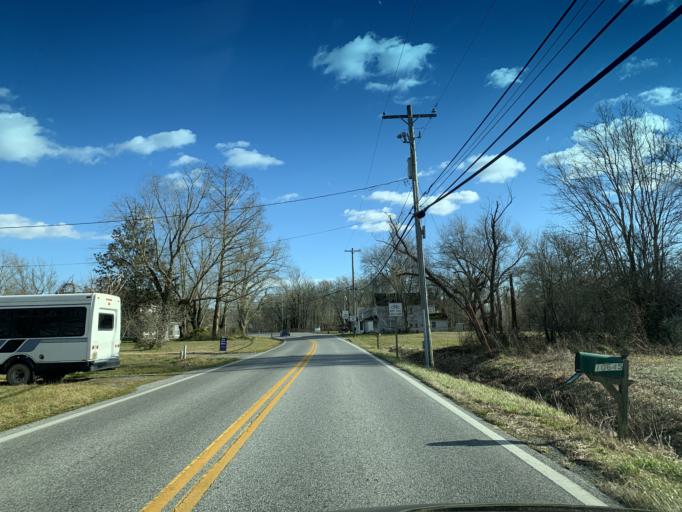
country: US
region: Maryland
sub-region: Worcester County
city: Berlin
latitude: 38.3152
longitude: -75.1945
